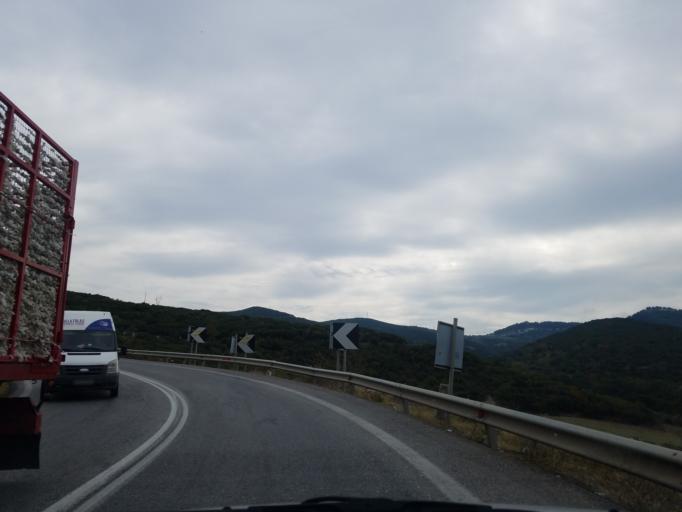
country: GR
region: Central Greece
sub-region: Nomos Fthiotidos
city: Domokos
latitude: 39.1539
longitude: 22.2952
